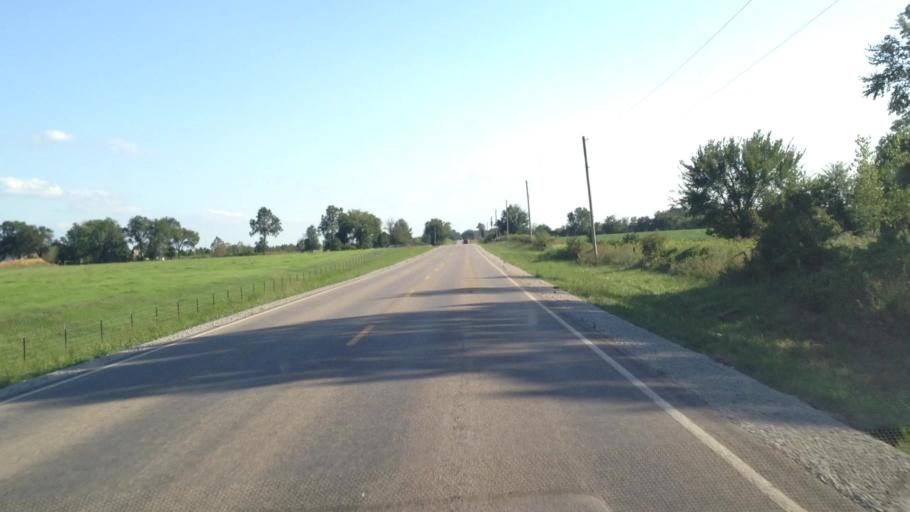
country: US
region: Kansas
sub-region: Crawford County
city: Pittsburg
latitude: 37.3490
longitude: -94.6316
